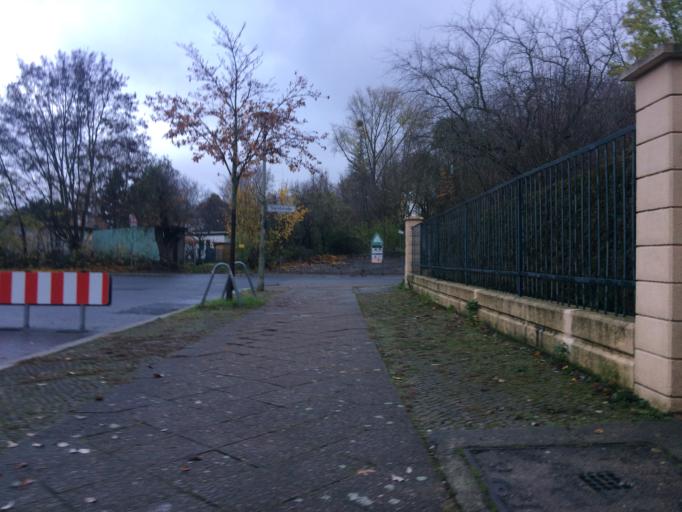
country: DE
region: Berlin
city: Fennpfuhl
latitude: 52.5355
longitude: 13.4583
